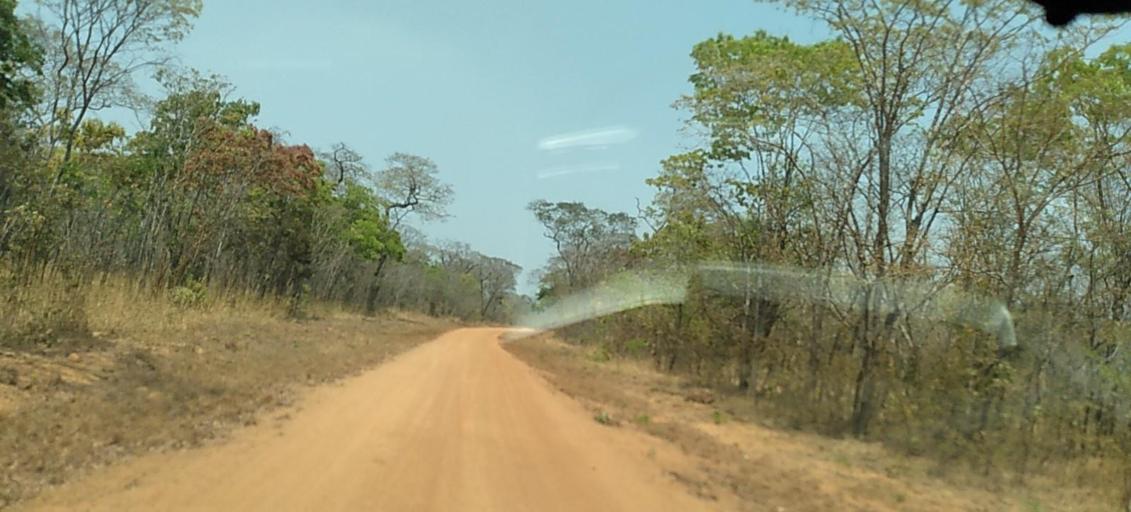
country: ZM
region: Central
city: Mumbwa
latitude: -14.3739
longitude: 26.4805
